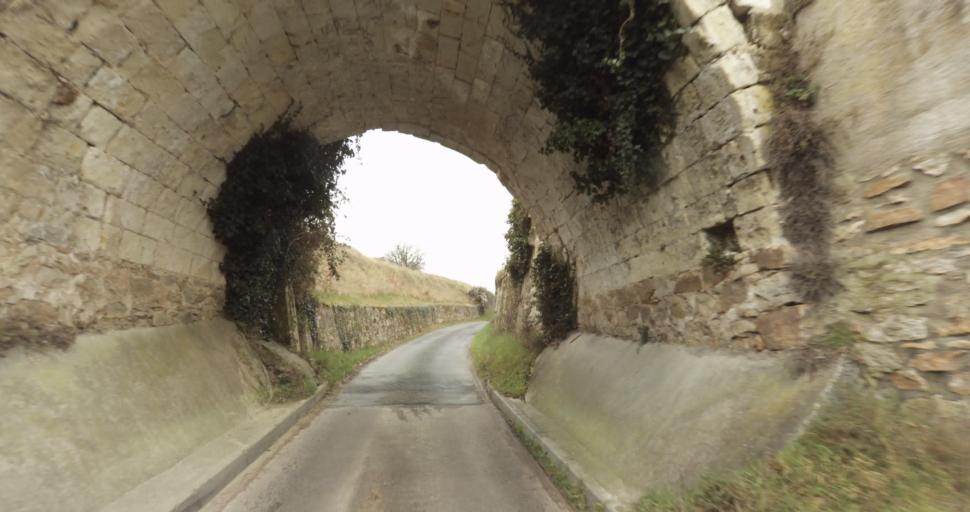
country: FR
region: Pays de la Loire
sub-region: Departement de Maine-et-Loire
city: Saumur
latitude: 47.2710
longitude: -0.1086
